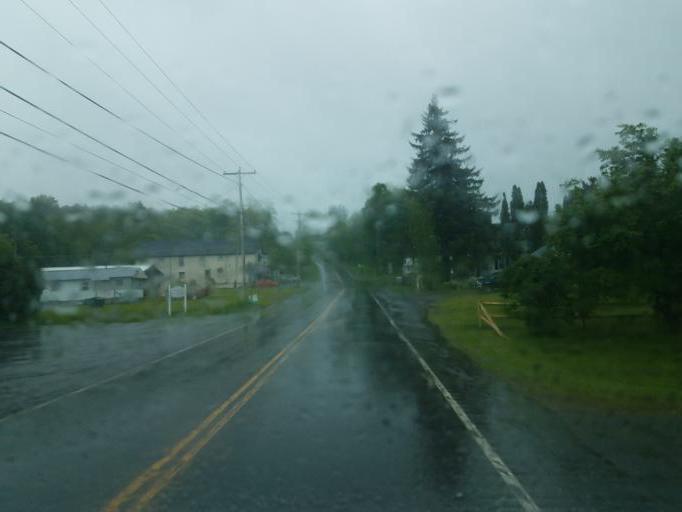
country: US
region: New York
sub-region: Herkimer County
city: Ilion
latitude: 42.9308
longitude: -75.1139
